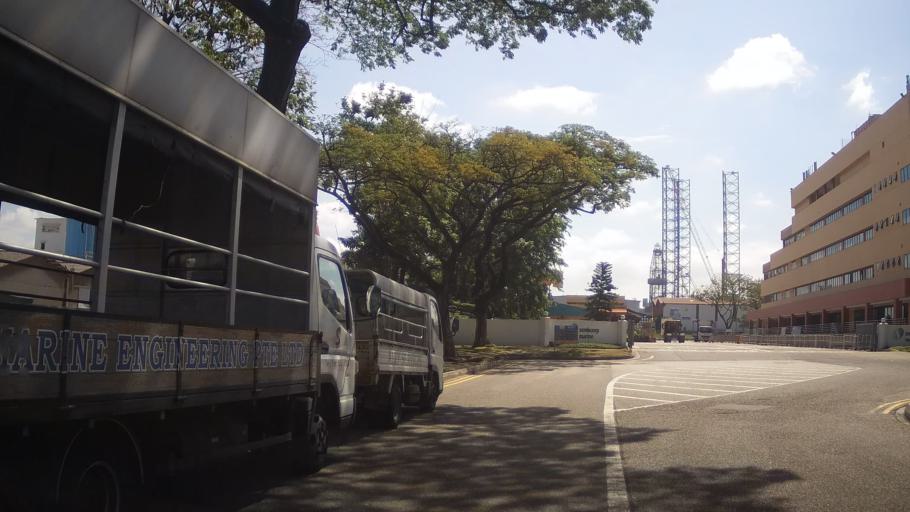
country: SG
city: Singapore
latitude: 1.3050
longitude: 103.7033
